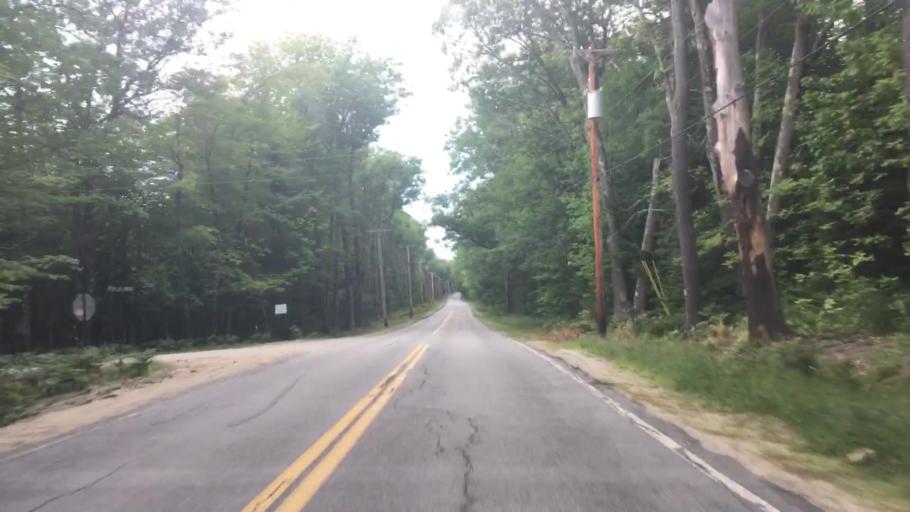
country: US
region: Maine
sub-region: Oxford County
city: Oxford
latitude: 44.0343
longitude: -70.5344
